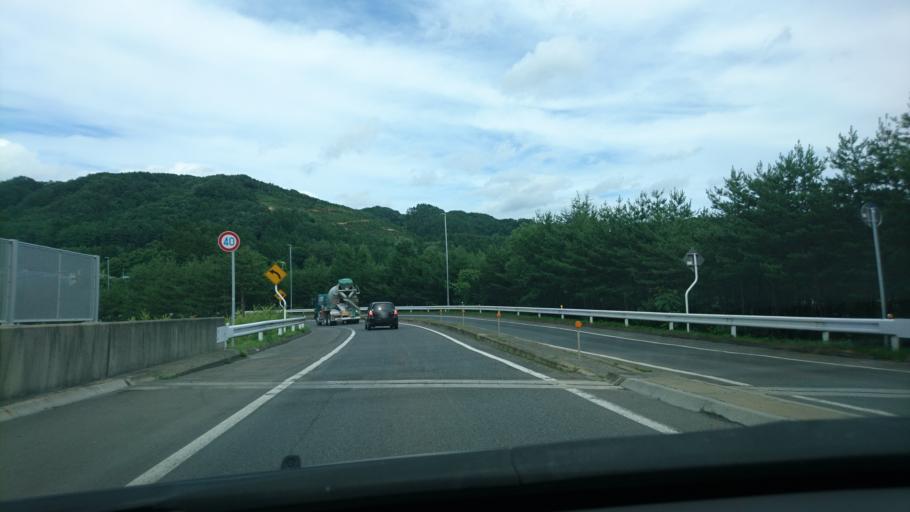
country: JP
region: Aomori
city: Hachinohe
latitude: 40.2216
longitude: 141.7831
